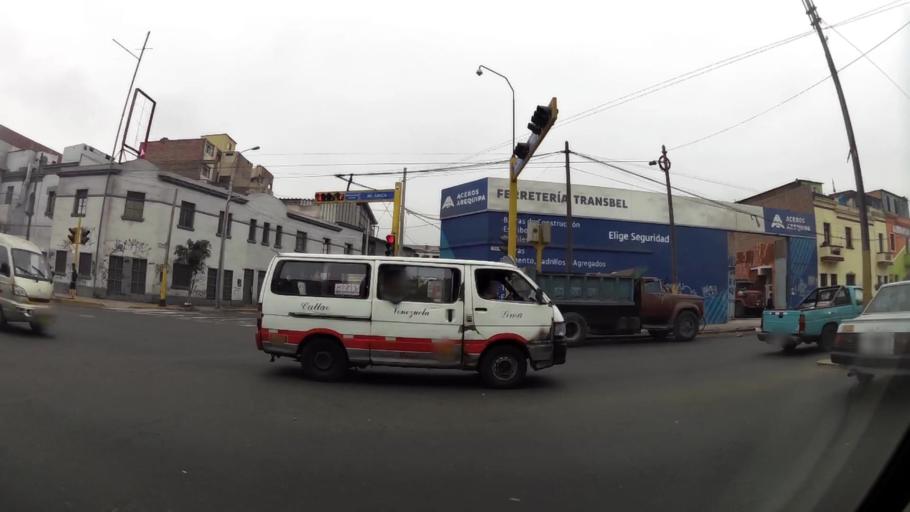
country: PE
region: Lima
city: Lima
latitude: -12.0568
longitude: -77.0531
